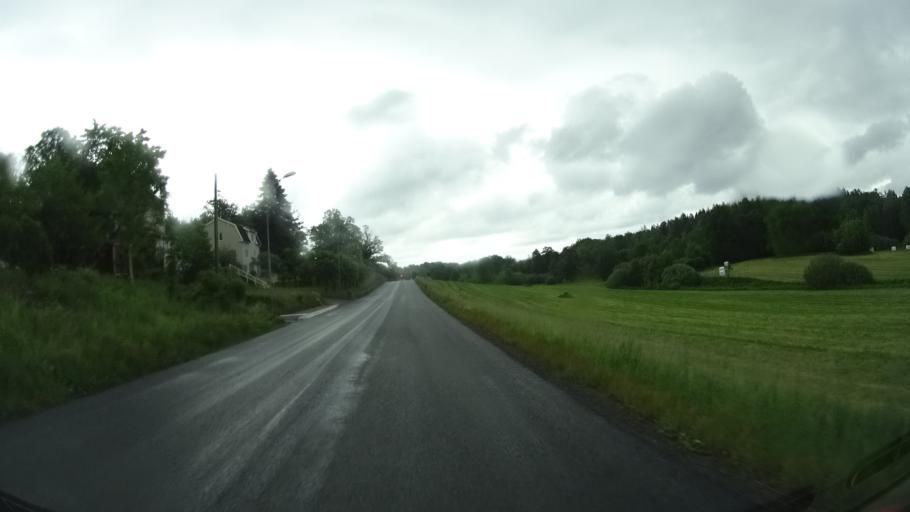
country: SE
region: Kalmar
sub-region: Oskarshamns Kommun
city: Oskarshamn
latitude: 57.3972
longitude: 16.2013
